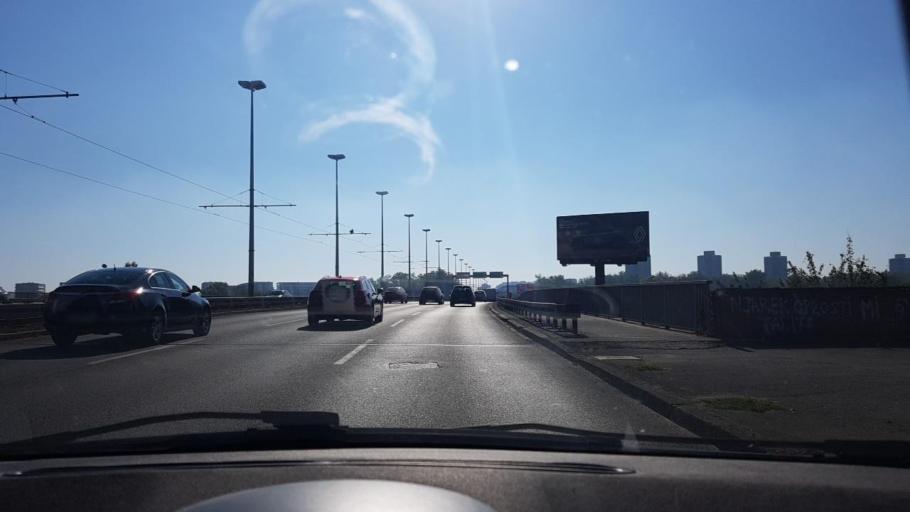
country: HR
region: Grad Zagreb
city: Novi Zagreb
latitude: 45.7867
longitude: 16.0050
